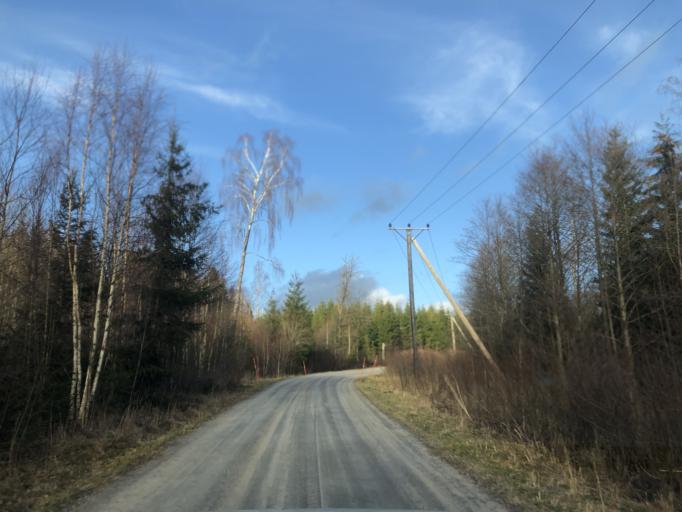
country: SE
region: Vaestra Goetaland
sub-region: Ulricehamns Kommun
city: Ulricehamn
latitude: 57.7618
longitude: 13.4598
